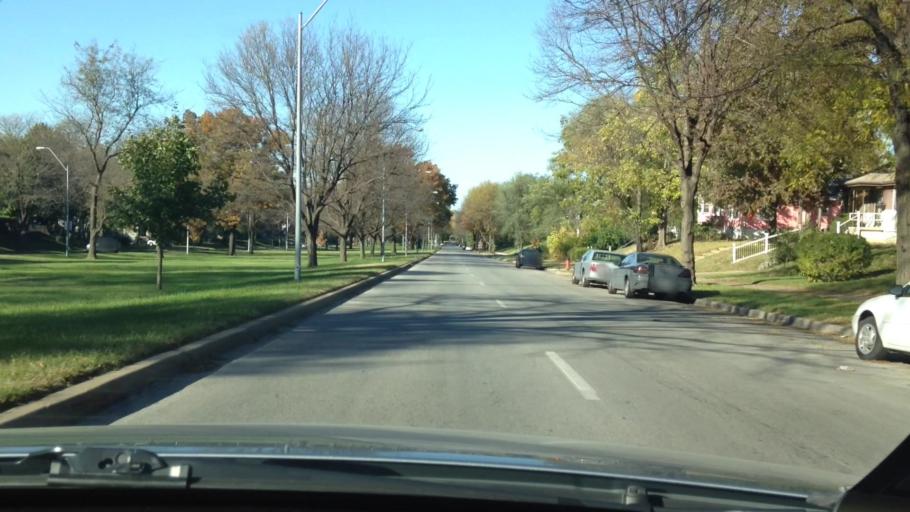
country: US
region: Kansas
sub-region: Johnson County
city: Westwood
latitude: 39.0309
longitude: -94.5673
